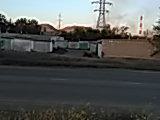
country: RU
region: Orenburg
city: Novotroitsk
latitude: 51.2074
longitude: 58.3086
